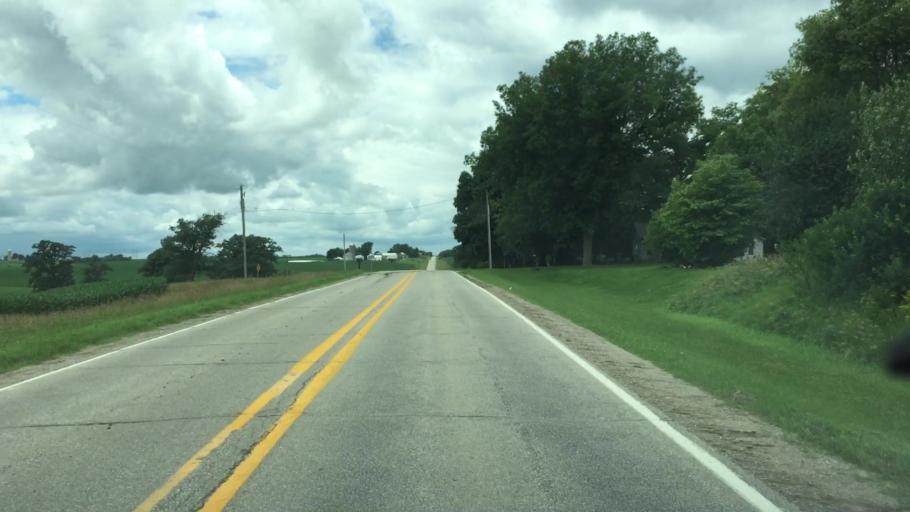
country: US
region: Iowa
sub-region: Jasper County
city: Monroe
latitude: 41.5735
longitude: -93.0483
